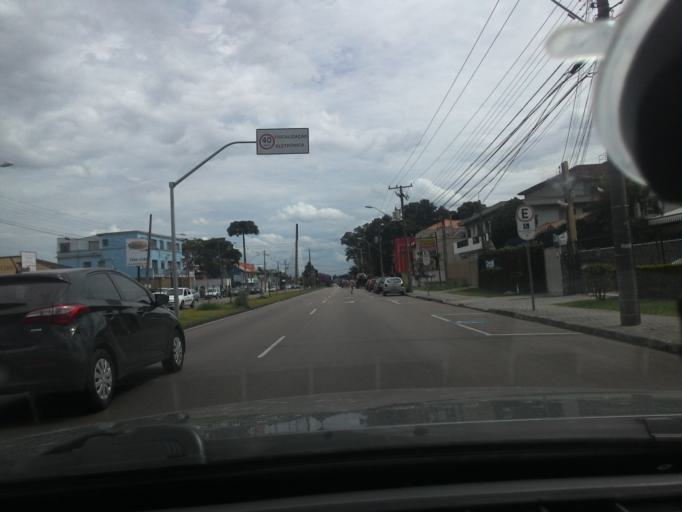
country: BR
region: Parana
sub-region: Pinhais
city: Pinhais
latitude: -25.4593
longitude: -49.2330
